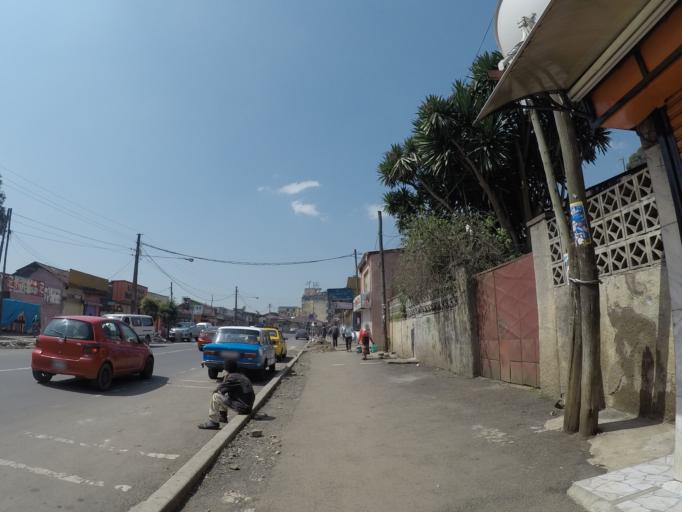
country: ET
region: Adis Abeba
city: Addis Ababa
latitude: 9.0368
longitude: 38.7533
